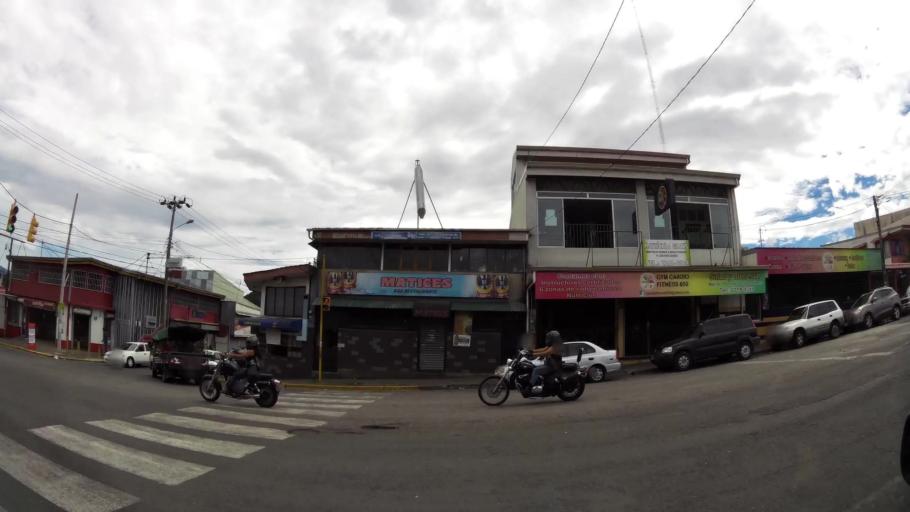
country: CR
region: San Jose
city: San Miguel
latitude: 9.8925
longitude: -84.0585
